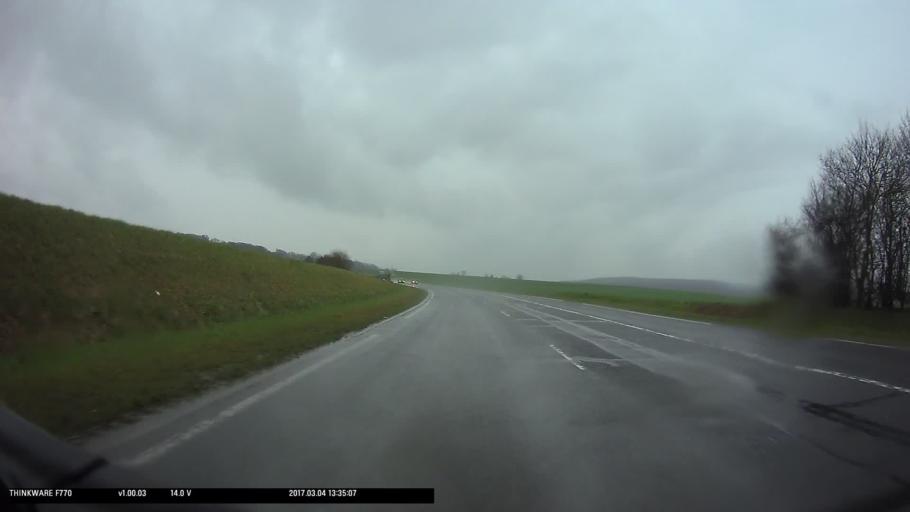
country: FR
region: Ile-de-France
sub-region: Departement du Val-d'Oise
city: Marines
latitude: 49.1210
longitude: 2.0266
